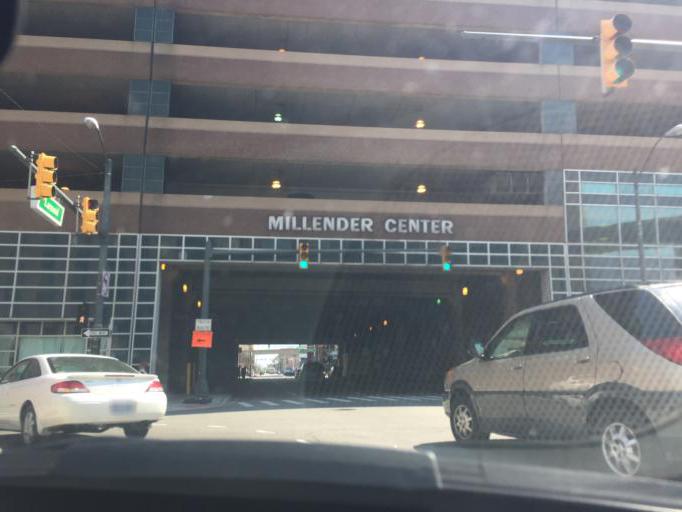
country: US
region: Michigan
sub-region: Wayne County
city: Detroit
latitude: 42.3306
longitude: -83.0427
